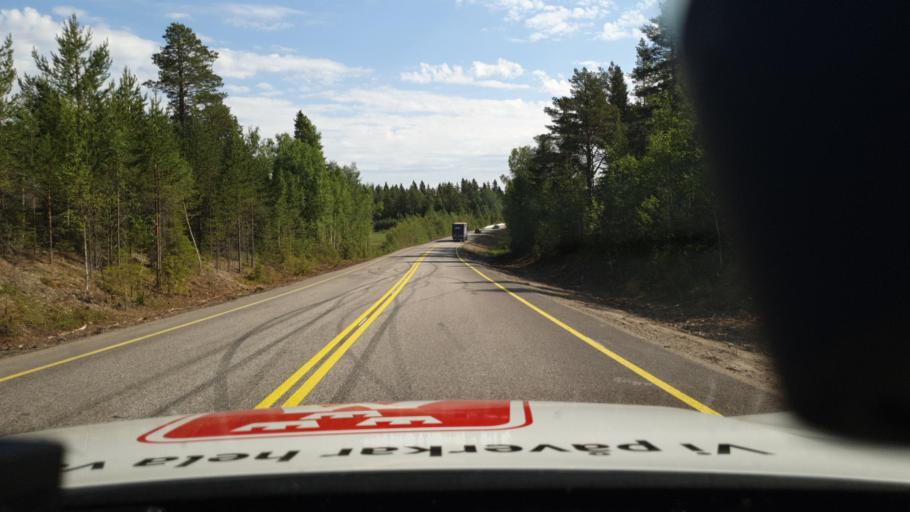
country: SE
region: Norrbotten
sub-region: Lulea Kommun
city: Ranea
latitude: 65.8702
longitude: 22.3354
